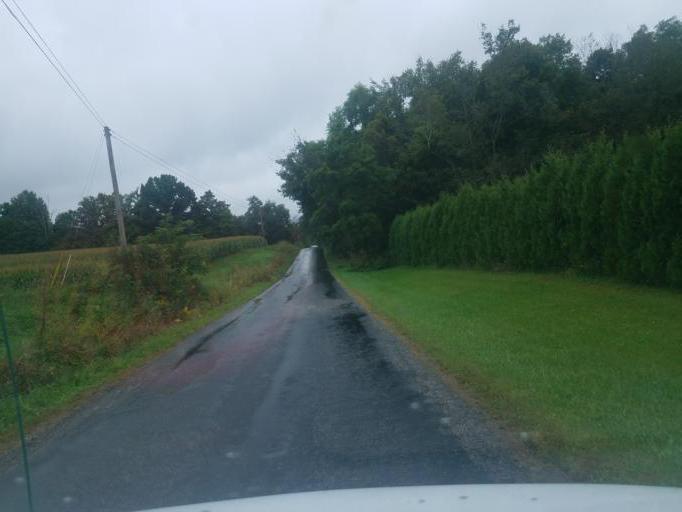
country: US
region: Ohio
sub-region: Wayne County
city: West Salem
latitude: 40.9202
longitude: -82.1528
